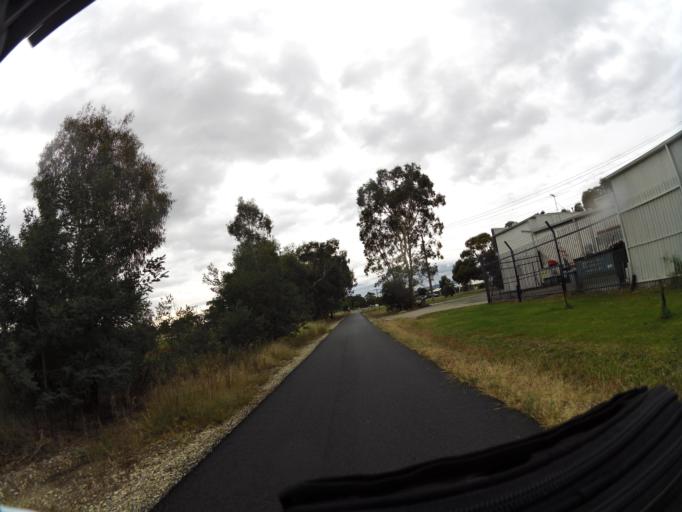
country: AU
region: Victoria
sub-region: Wodonga
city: Wodonga
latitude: -36.1312
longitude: 146.8977
